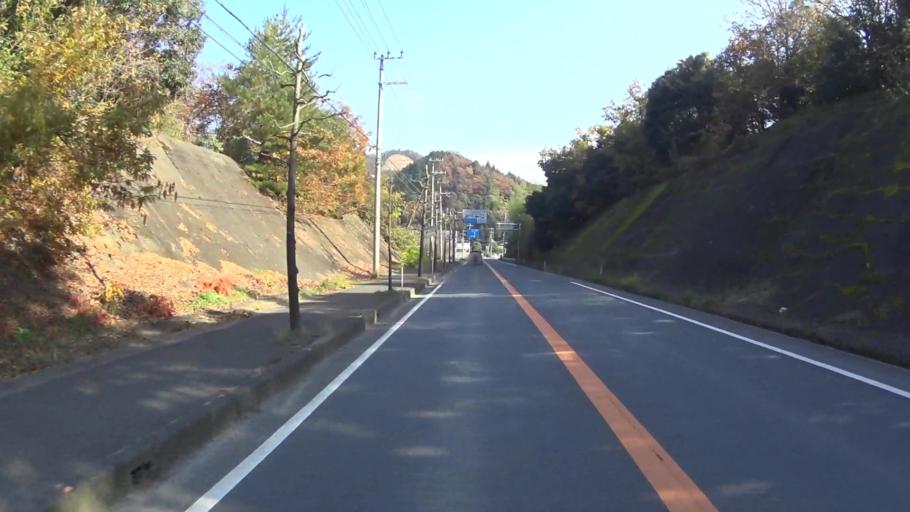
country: JP
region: Kyoto
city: Maizuru
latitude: 35.4292
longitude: 135.2280
